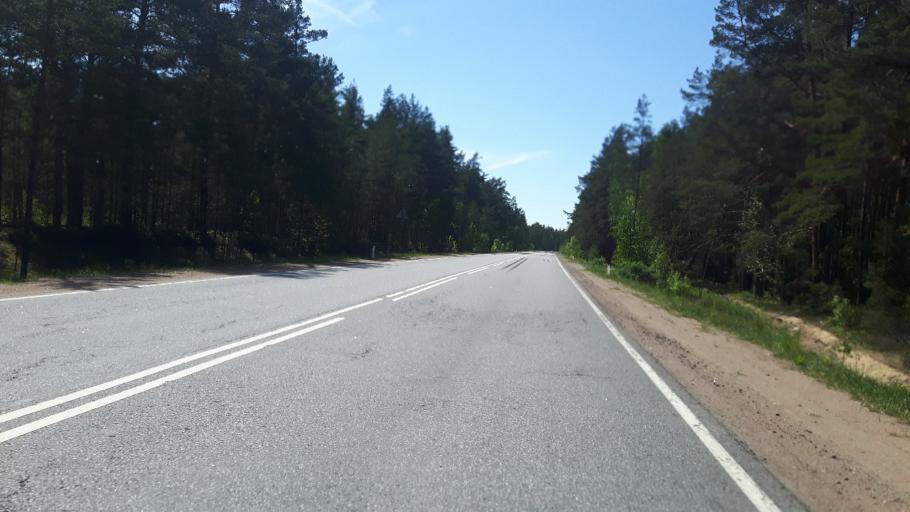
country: RU
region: Leningrad
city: Sista-Palkino
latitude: 59.7677
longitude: 28.8105
